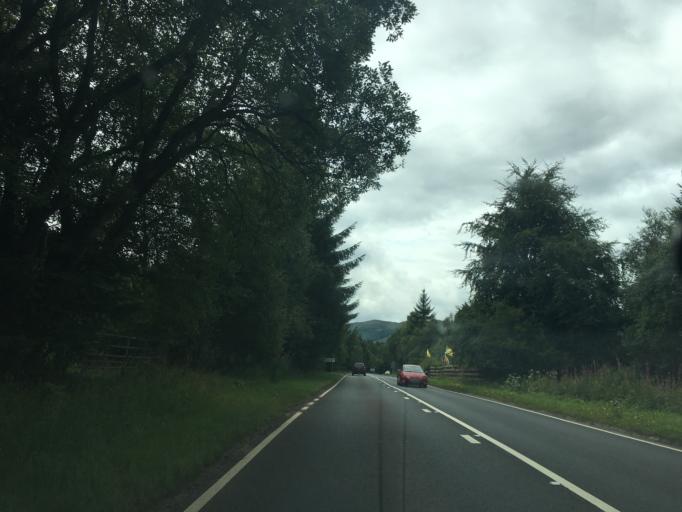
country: GB
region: Scotland
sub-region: Stirling
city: Callander
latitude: 56.3630
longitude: -4.3042
